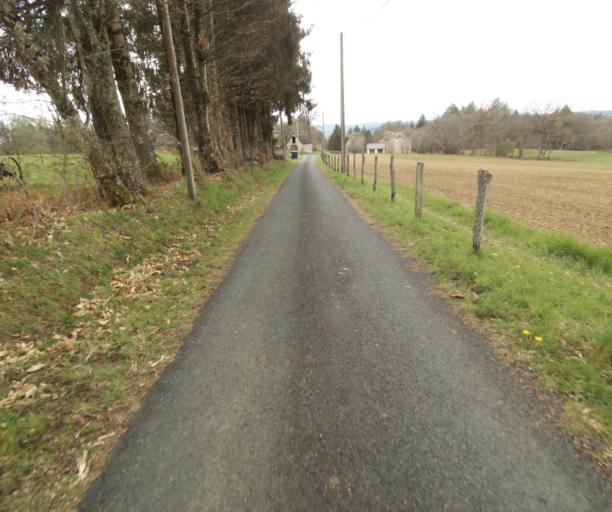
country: FR
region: Limousin
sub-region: Departement de la Correze
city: Laguenne
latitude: 45.2096
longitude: 1.8742
